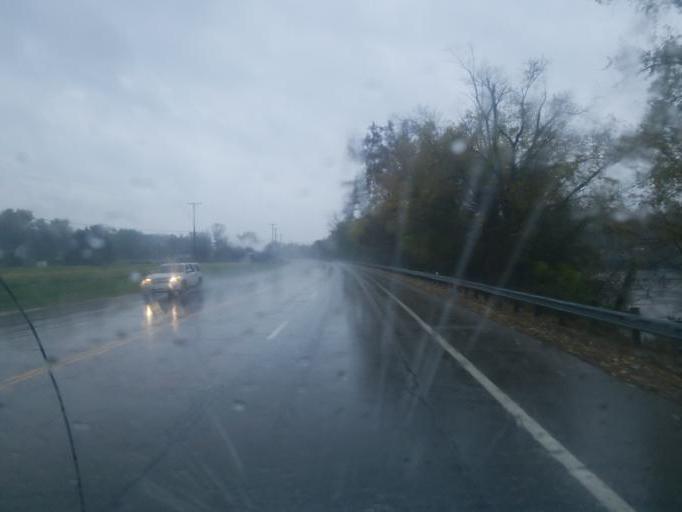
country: US
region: Ohio
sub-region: Muskingum County
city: South Zanesville
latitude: 39.8850
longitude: -81.9870
